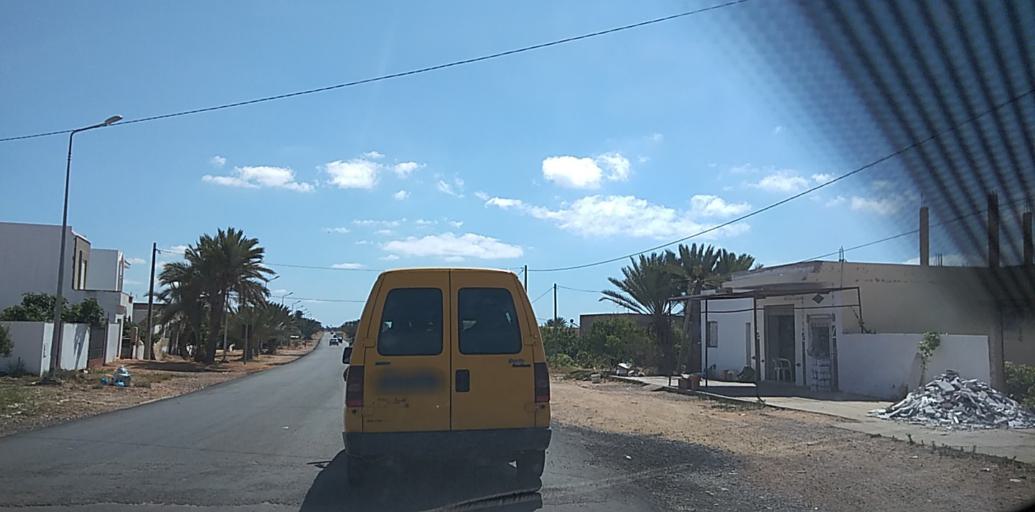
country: TN
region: Safaqis
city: Al Qarmadah
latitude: 34.6562
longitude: 11.0920
